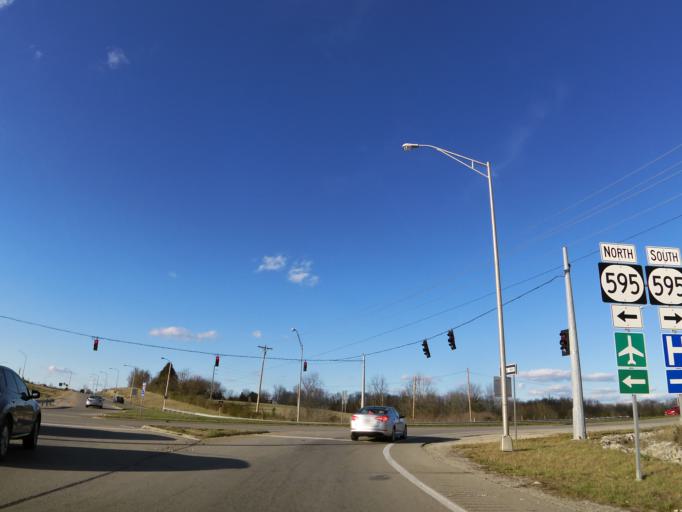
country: US
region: Kentucky
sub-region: Madison County
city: Berea
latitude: 37.5971
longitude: -84.3134
